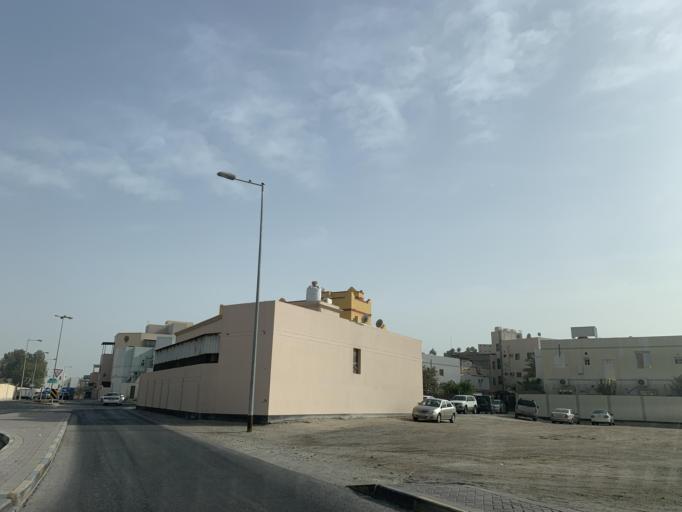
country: BH
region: Northern
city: Madinat `Isa
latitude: 26.1692
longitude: 50.5713
